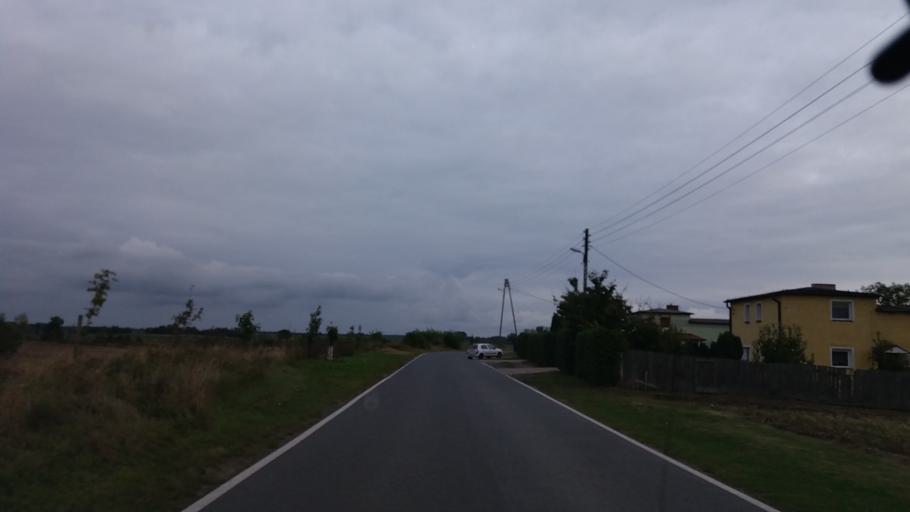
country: PL
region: West Pomeranian Voivodeship
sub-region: Powiat choszczenski
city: Pelczyce
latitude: 53.0297
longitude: 15.3553
